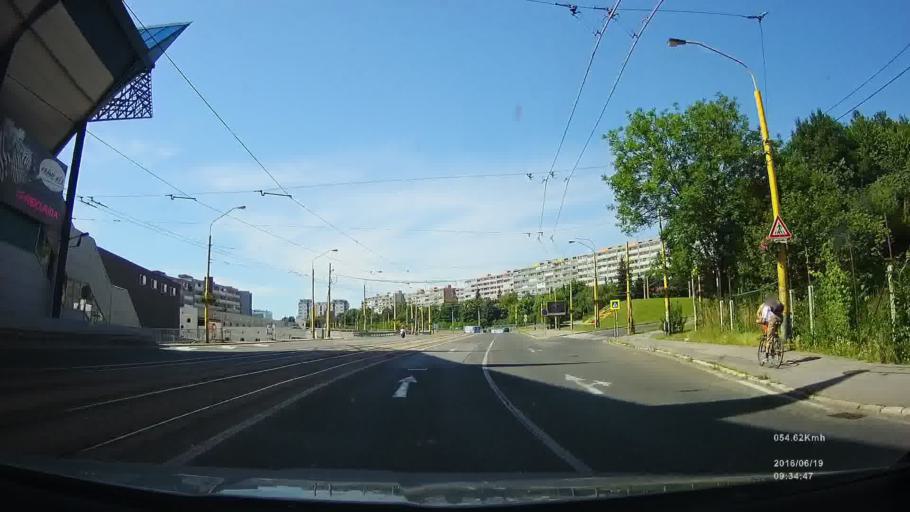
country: SK
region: Kosicky
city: Kosice
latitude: 48.7153
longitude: 21.2474
